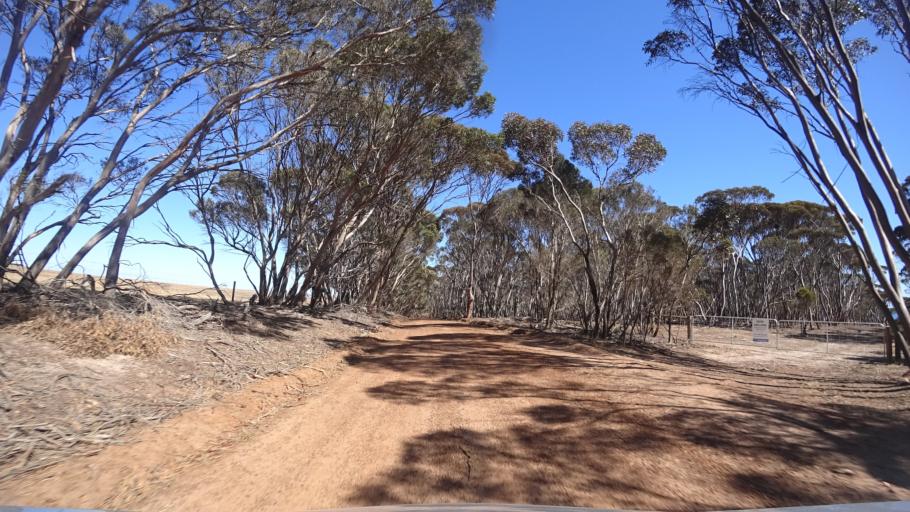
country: AU
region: South Australia
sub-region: Kangaroo Island
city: Kingscote
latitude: -35.7480
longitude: 137.7263
